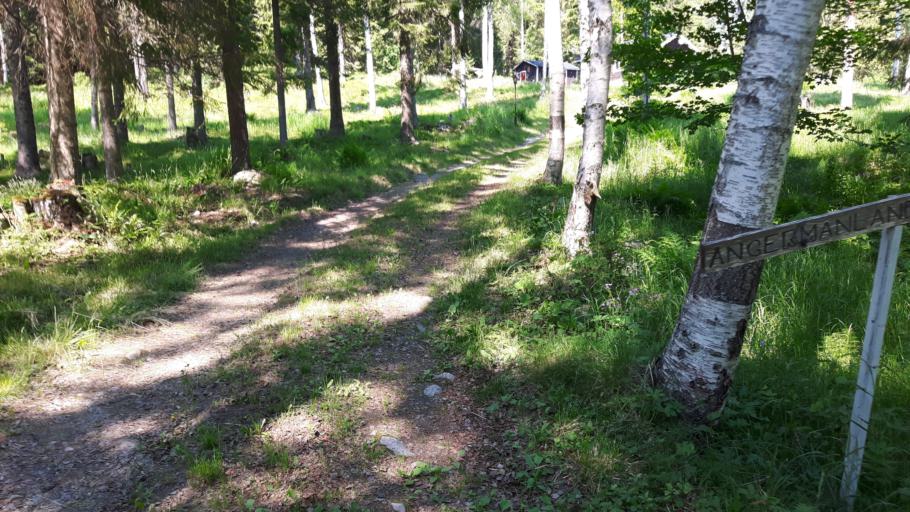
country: SE
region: Vaesternorrland
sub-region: Timra Kommun
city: Soraker
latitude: 62.6498
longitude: 17.5165
